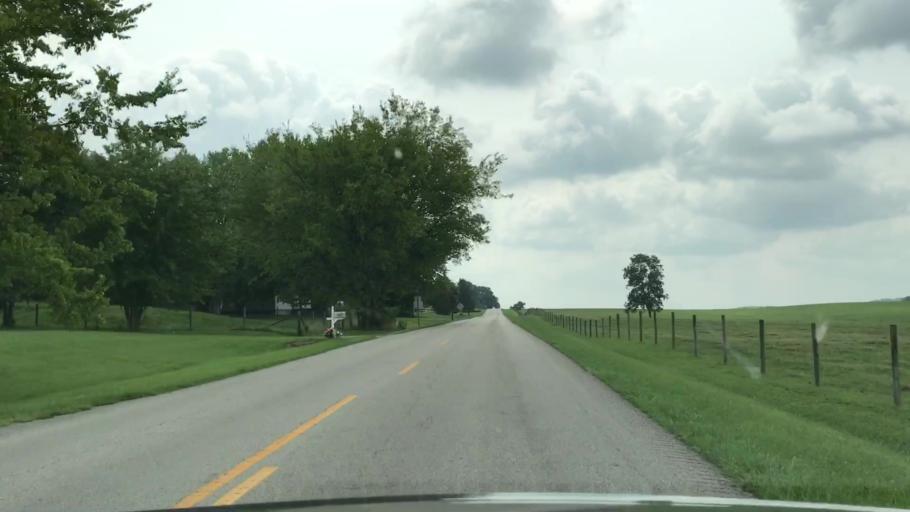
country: US
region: Kentucky
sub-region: Barren County
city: Cave City
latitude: 37.1110
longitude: -85.9865
